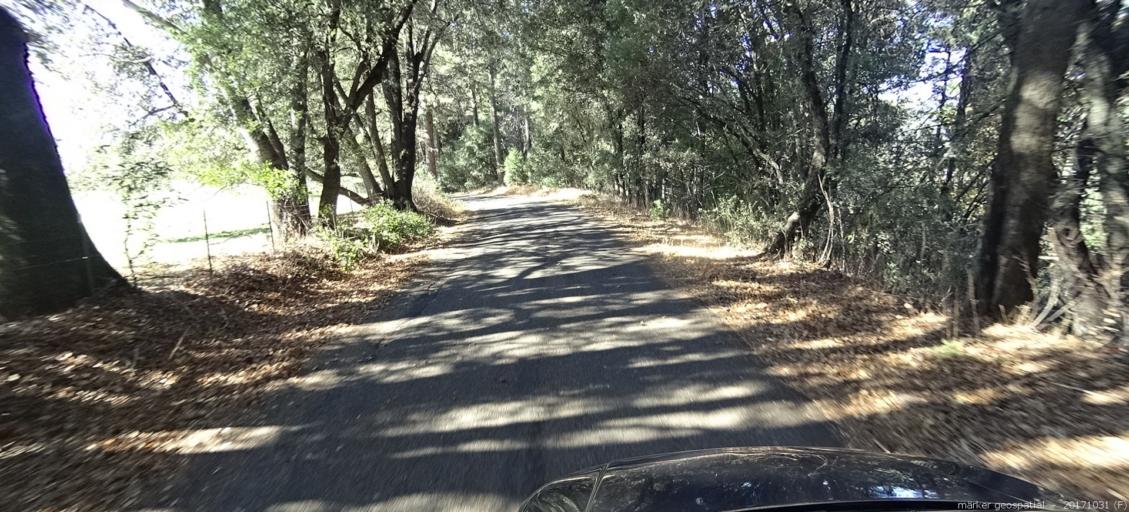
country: US
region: California
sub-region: Shasta County
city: Shingletown
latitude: 40.5306
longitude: -121.9502
